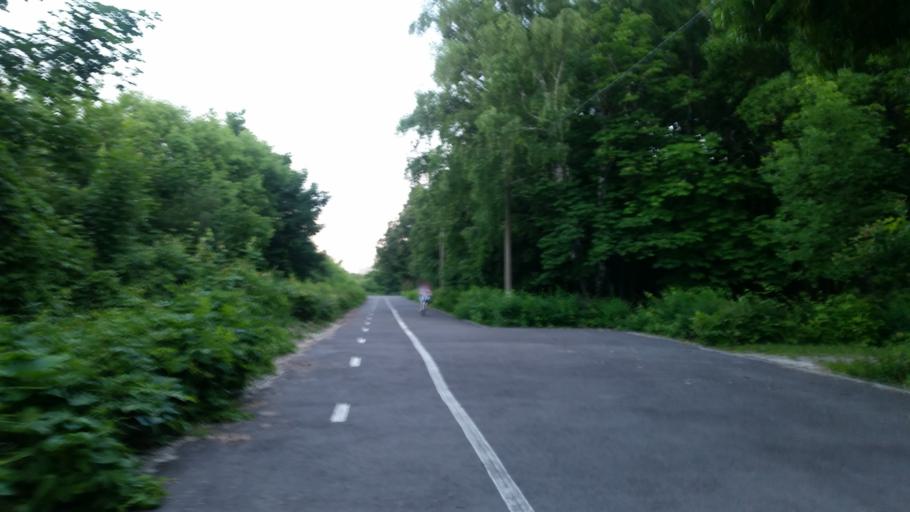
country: RU
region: Ulyanovsk
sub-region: Ulyanovskiy Rayon
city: Ulyanovsk
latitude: 54.3329
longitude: 48.4071
